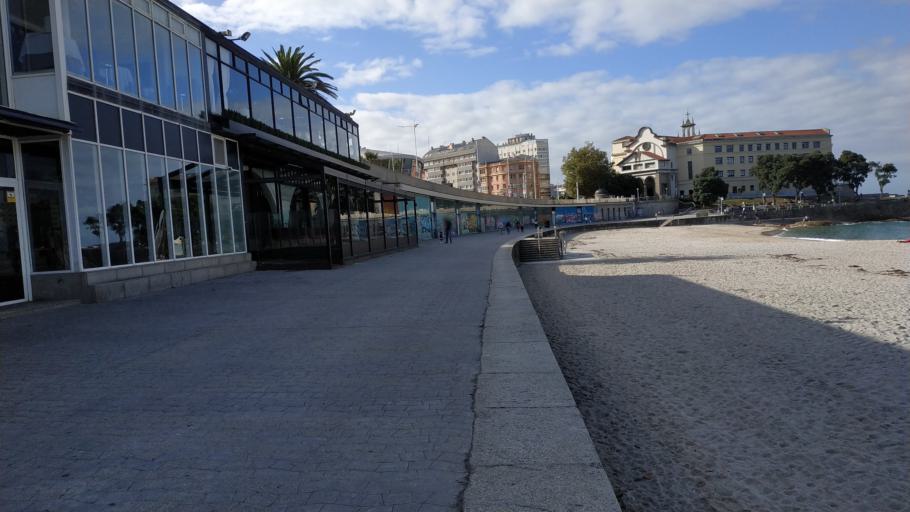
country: ES
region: Galicia
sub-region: Provincia da Coruna
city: A Coruna
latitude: 43.3686
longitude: -8.4134
